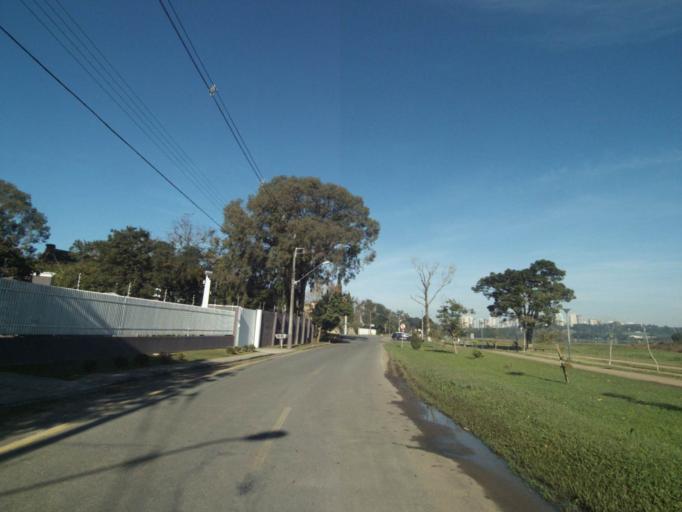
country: BR
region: Parana
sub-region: Curitiba
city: Curitiba
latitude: -25.4283
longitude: -49.3053
